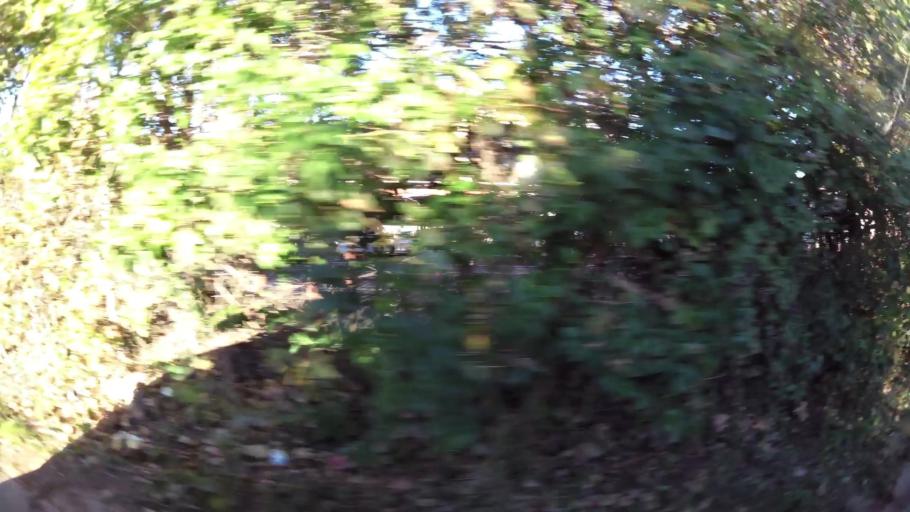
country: GR
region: Attica
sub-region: Nomarchia Anatolikis Attikis
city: Pallini
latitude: 37.9998
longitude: 23.8633
